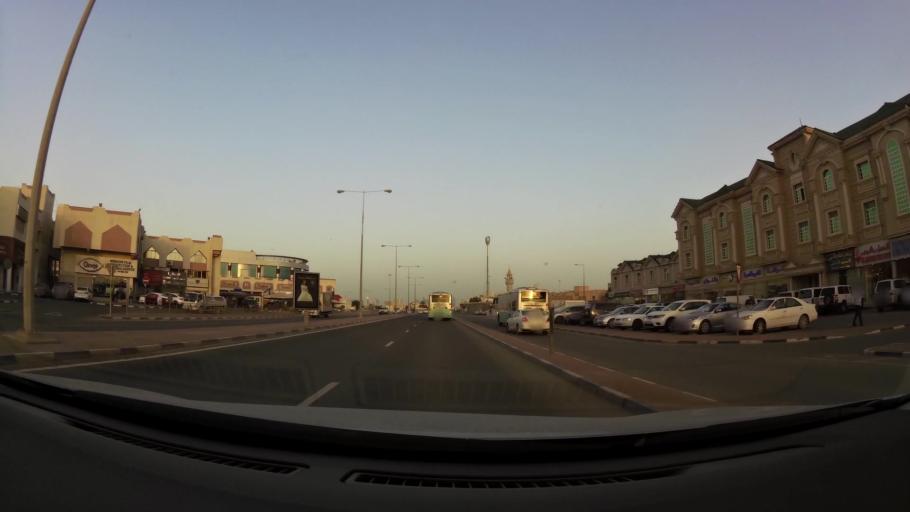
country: QA
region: Baladiyat ar Rayyan
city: Ar Rayyan
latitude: 25.3260
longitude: 51.4642
